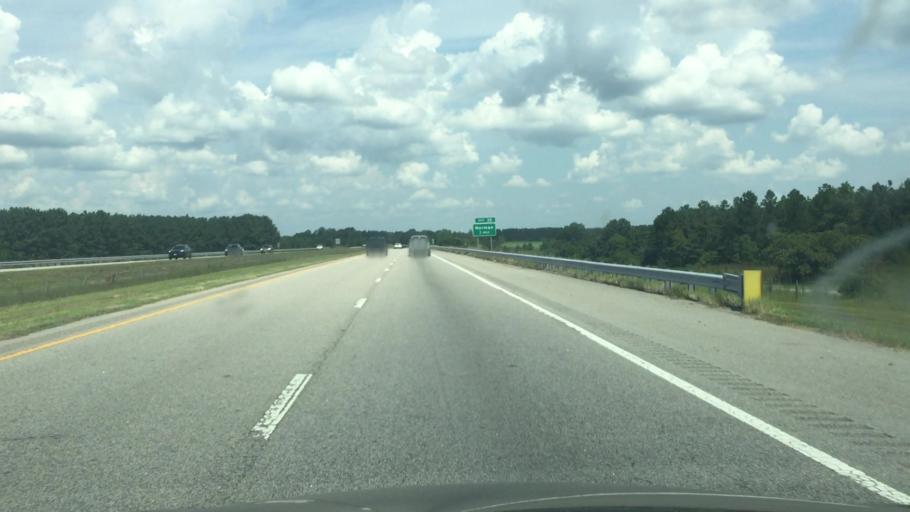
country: US
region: North Carolina
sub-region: Richmond County
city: Ellerbe
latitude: 35.1534
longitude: -79.7150
